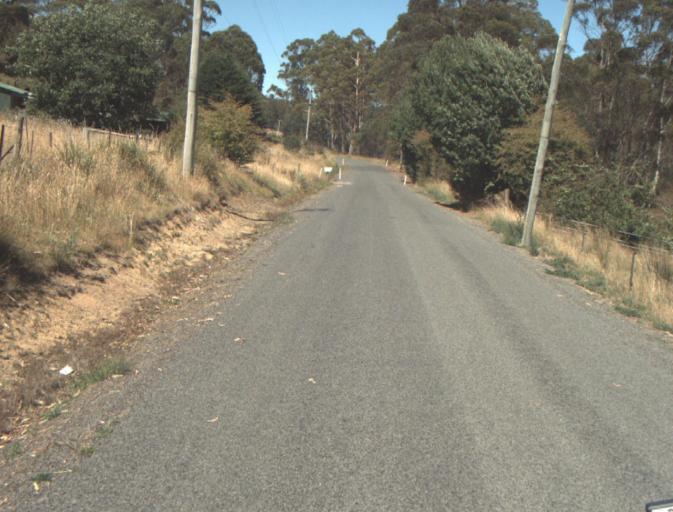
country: AU
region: Tasmania
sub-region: Launceston
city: Newstead
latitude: -41.3552
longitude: 147.3032
